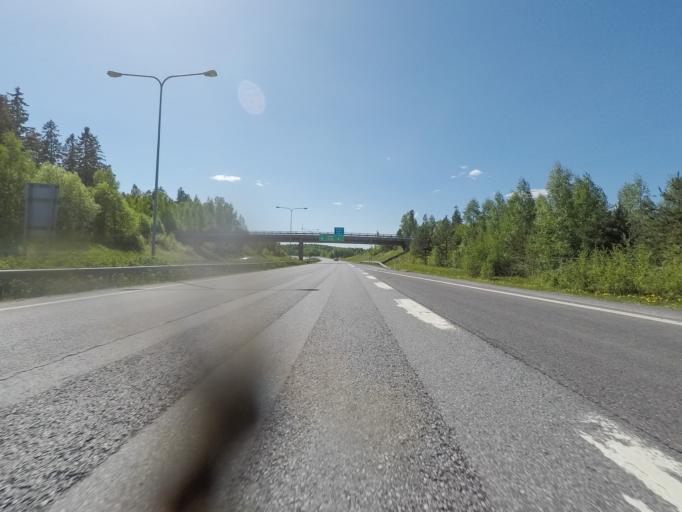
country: FI
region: Pirkanmaa
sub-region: Etelae-Pirkanmaa
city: Toijala
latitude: 61.2016
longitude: 23.8298
